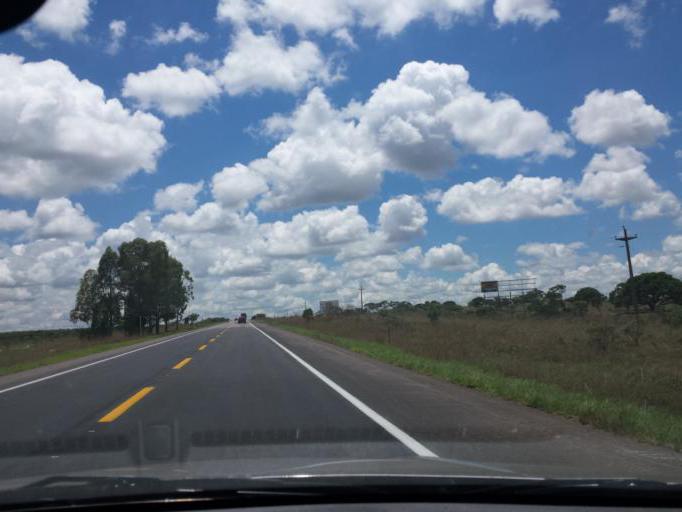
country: BR
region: Goias
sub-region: Cristalina
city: Cristalina
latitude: -16.7200
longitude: -47.6532
